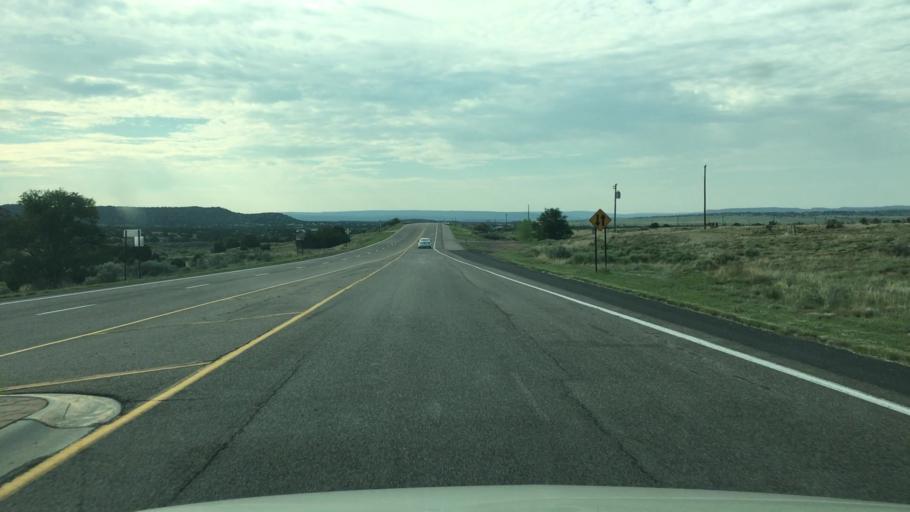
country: US
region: New Mexico
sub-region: Santa Fe County
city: Eldorado at Santa Fe
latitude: 35.4698
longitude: -105.9035
